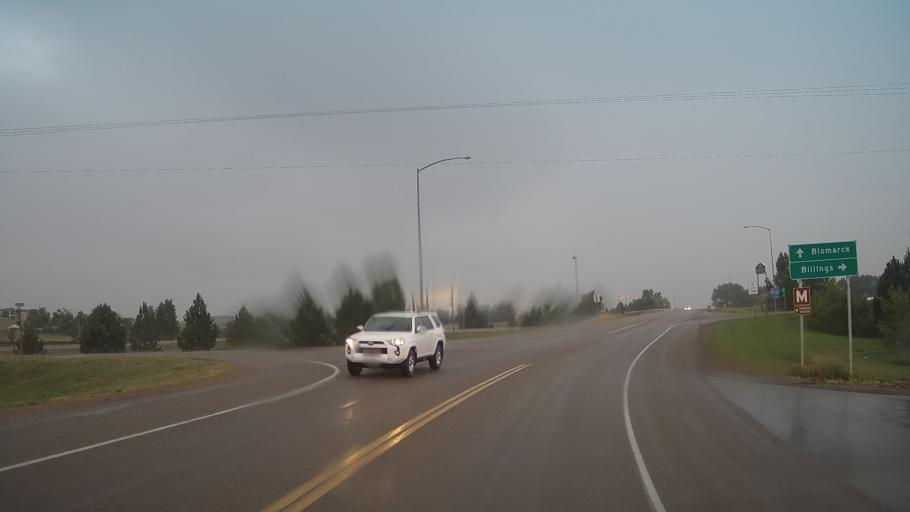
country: US
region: Montana
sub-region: Dawson County
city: Glendive
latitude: 47.1254
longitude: -104.6933
